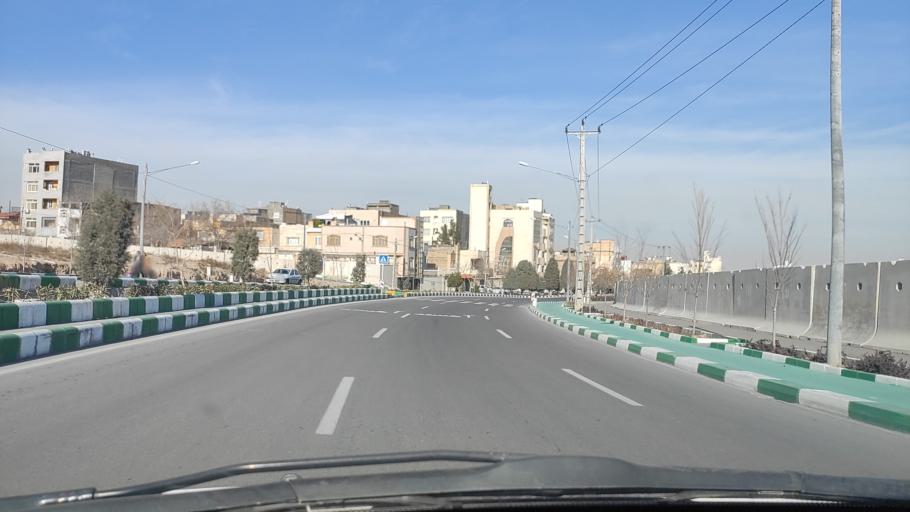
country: IR
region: Razavi Khorasan
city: Mashhad
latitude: 36.2848
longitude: 59.5311
